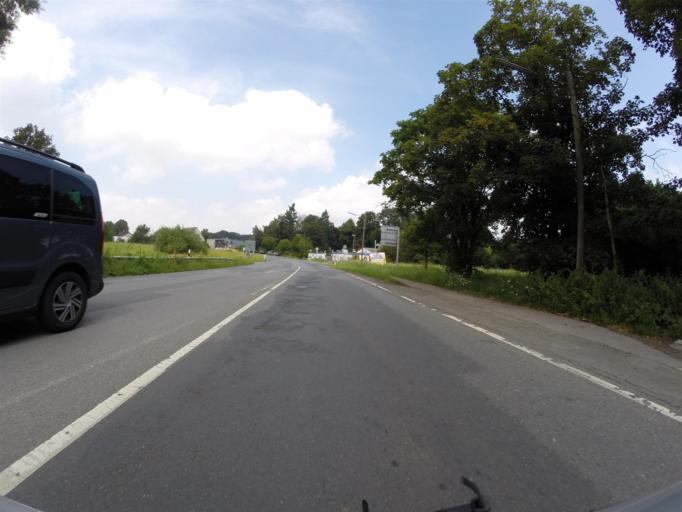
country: DE
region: North Rhine-Westphalia
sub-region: Regierungsbezirk Detmold
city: Herford
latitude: 52.1334
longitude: 8.6640
